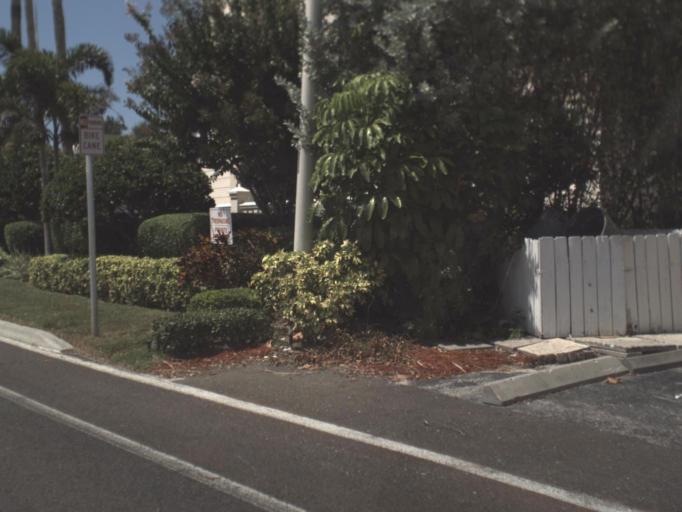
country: US
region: Florida
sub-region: Pinellas County
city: Indian Rocks Beach
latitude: 27.8692
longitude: -82.8494
